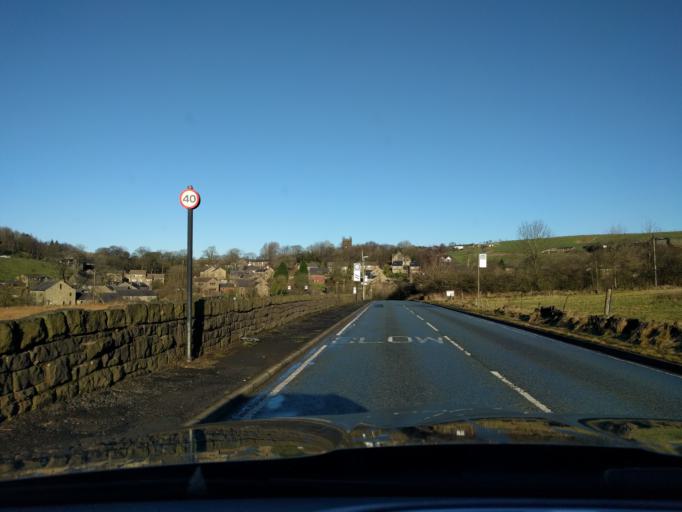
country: GB
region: England
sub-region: Borough of Oldham
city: Delph
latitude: 53.5877
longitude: -2.0383
